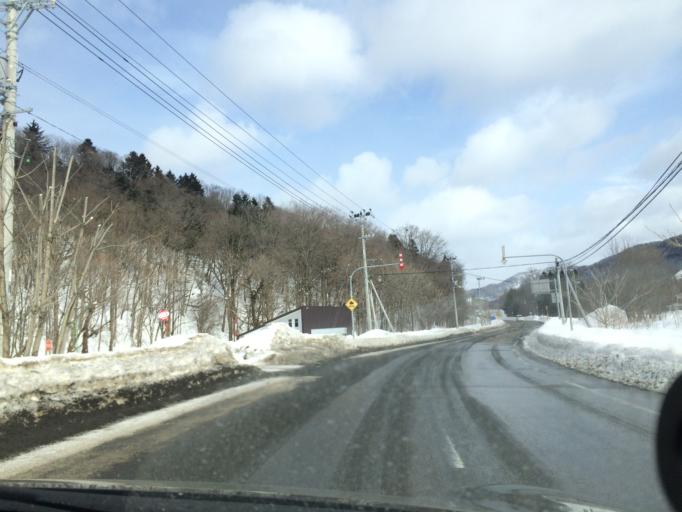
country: JP
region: Hokkaido
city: Shimo-furano
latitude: 43.0074
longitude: 142.4080
